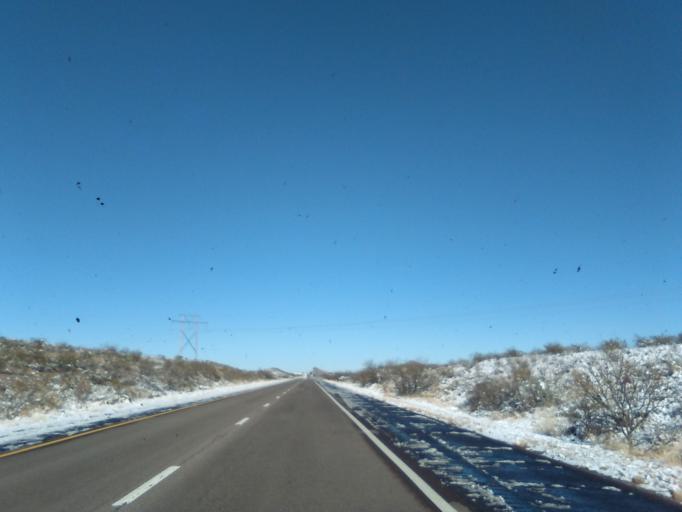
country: US
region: New Mexico
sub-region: Socorro County
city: Socorro
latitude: 33.7166
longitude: -107.0328
